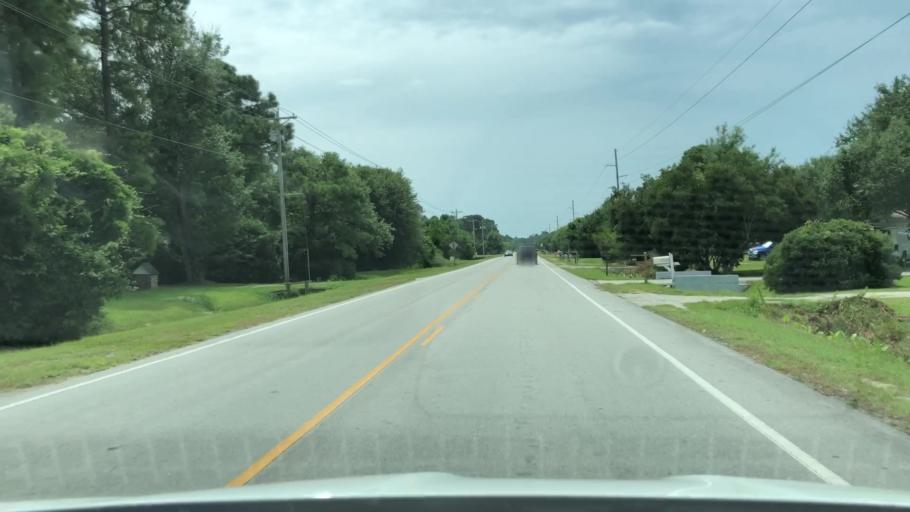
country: US
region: North Carolina
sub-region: Carteret County
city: Newport
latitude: 34.7410
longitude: -76.8841
